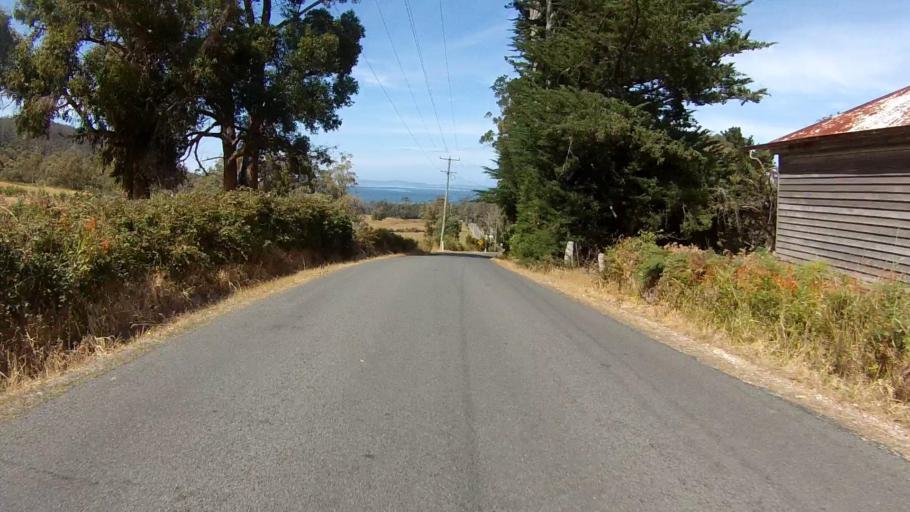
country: AU
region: Tasmania
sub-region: Huon Valley
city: Cygnet
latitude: -43.2333
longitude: 147.1263
